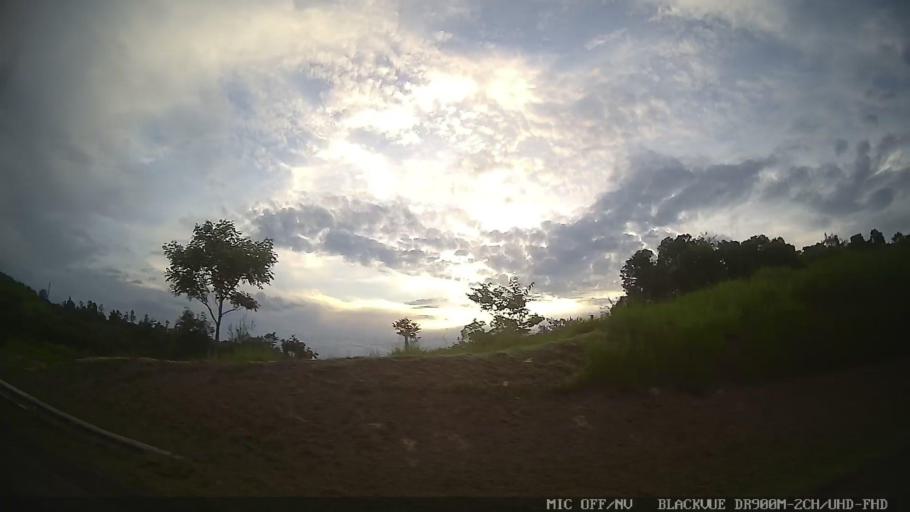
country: BR
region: Sao Paulo
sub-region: Itu
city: Itu
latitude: -23.2611
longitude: -47.2703
